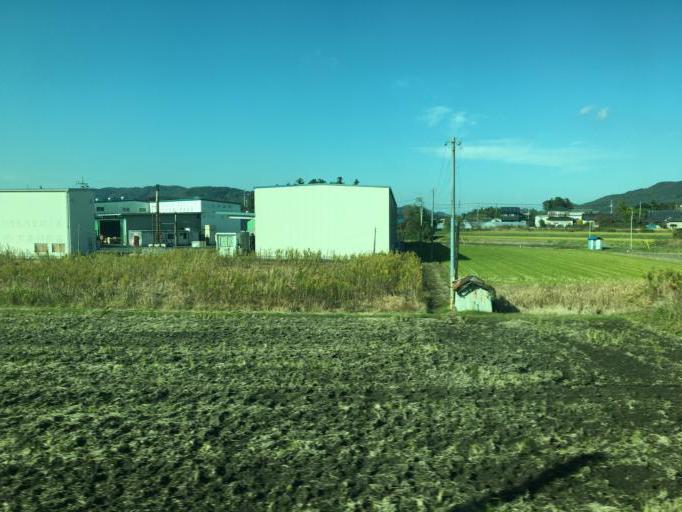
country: JP
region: Ibaraki
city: Iwase
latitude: 36.3568
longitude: 140.0948
